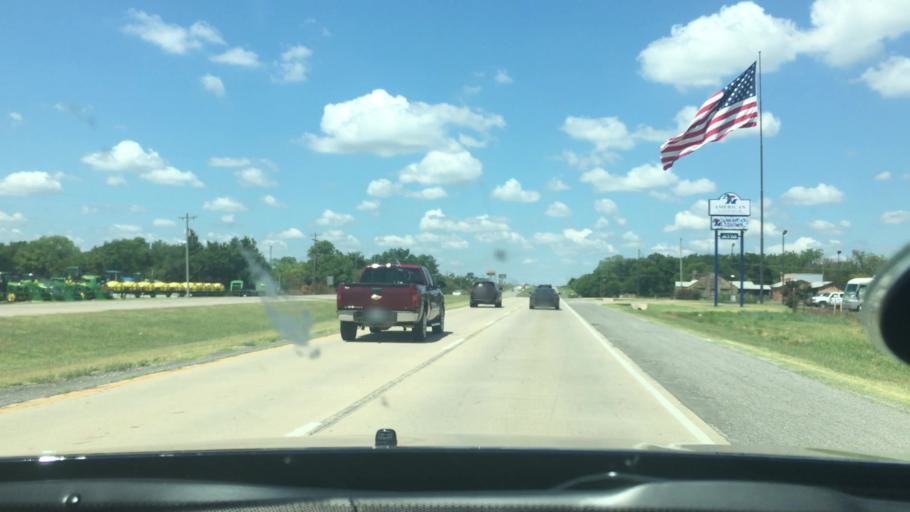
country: US
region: Oklahoma
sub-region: Carter County
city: Lone Grove
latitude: 34.1731
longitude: -97.2088
